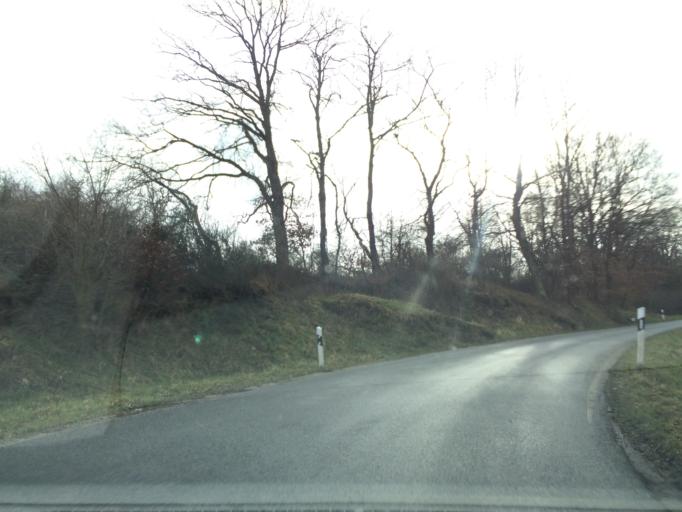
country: DE
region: Hesse
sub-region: Regierungsbezirk Darmstadt
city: Gravenwiesbach
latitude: 50.3593
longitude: 8.4319
